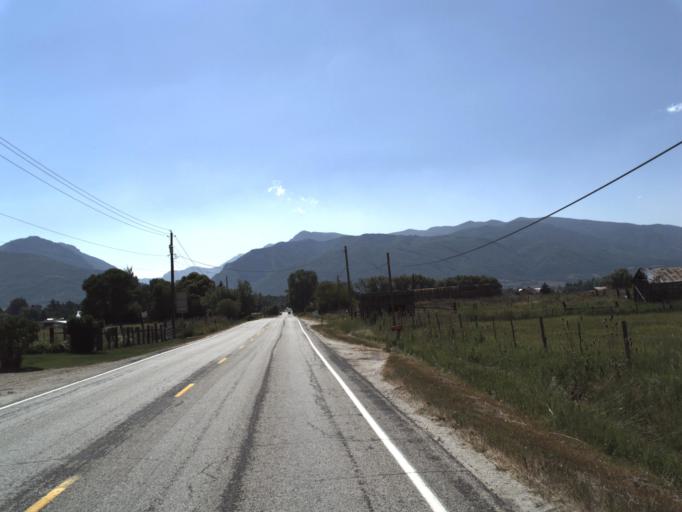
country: US
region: Utah
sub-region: Weber County
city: Wolf Creek
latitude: 41.2622
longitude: -111.7471
